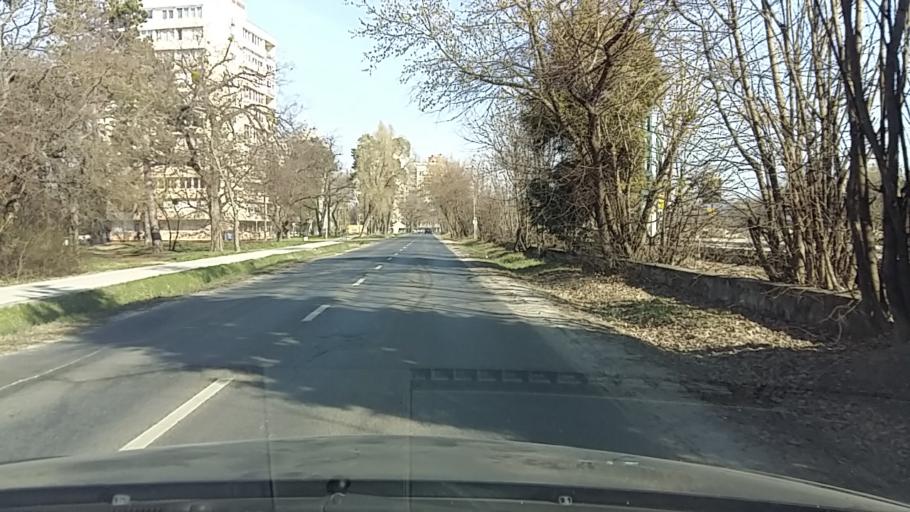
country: HU
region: Pest
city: Godollo
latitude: 47.5939
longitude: 19.3574
